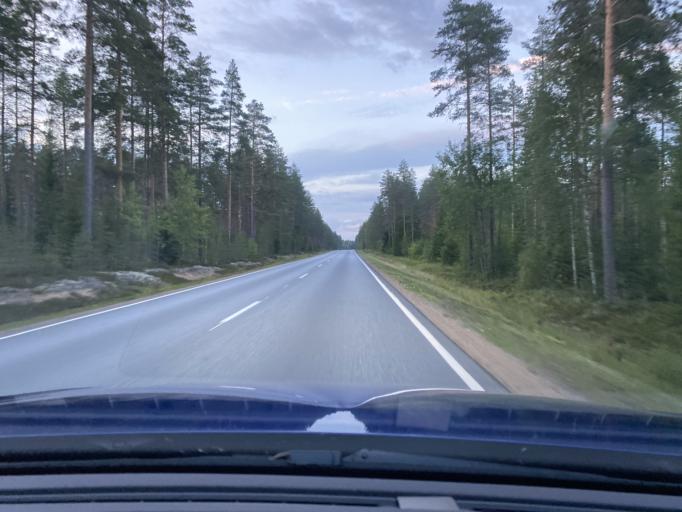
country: FI
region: Satakunta
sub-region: Pohjois-Satakunta
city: Honkajoki
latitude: 62.1372
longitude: 22.2527
